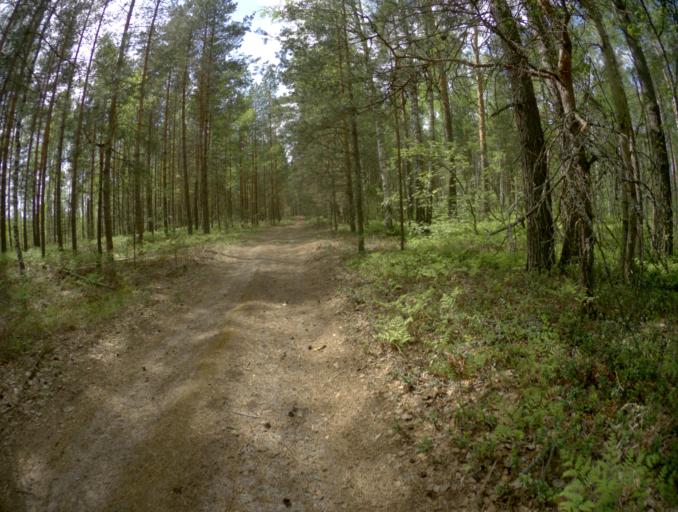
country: RU
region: Vladimir
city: Ivanishchi
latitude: 55.6910
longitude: 40.4203
